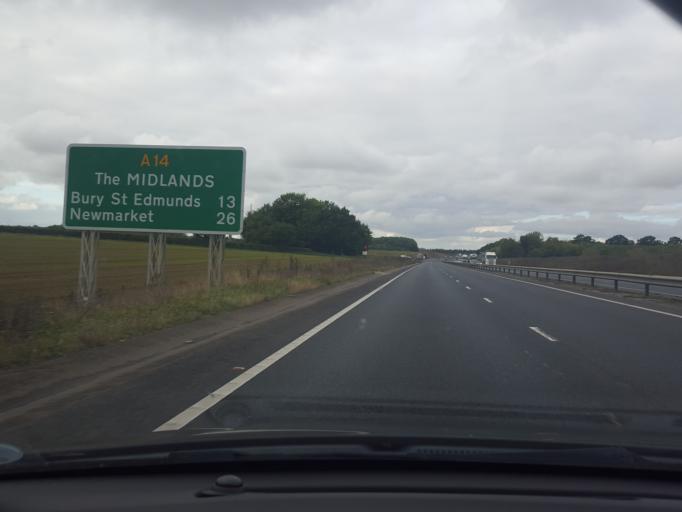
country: GB
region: England
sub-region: Suffolk
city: Stowmarket
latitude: 52.2103
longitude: 0.9660
